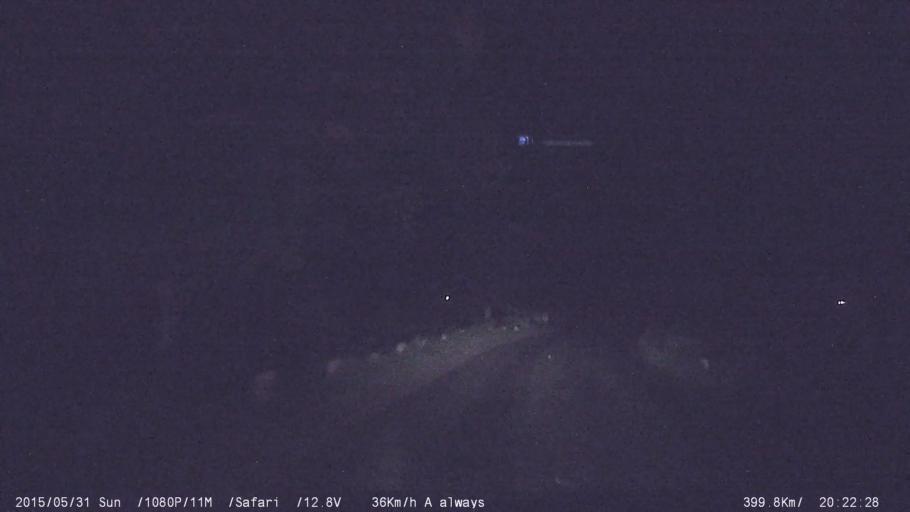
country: IN
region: Karnataka
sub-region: Mandya
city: Malavalli
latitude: 12.4259
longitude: 77.2195
